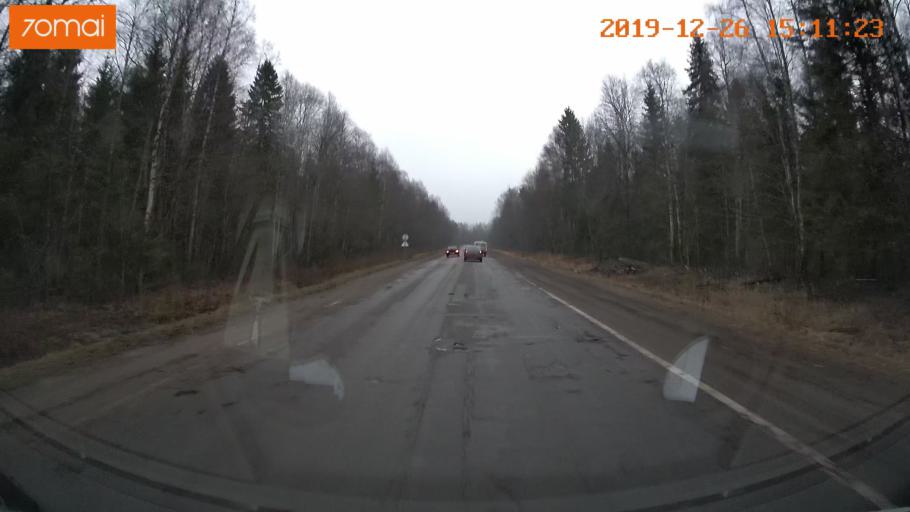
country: RU
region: Jaroslavl
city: Rybinsk
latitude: 58.1348
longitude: 38.8609
